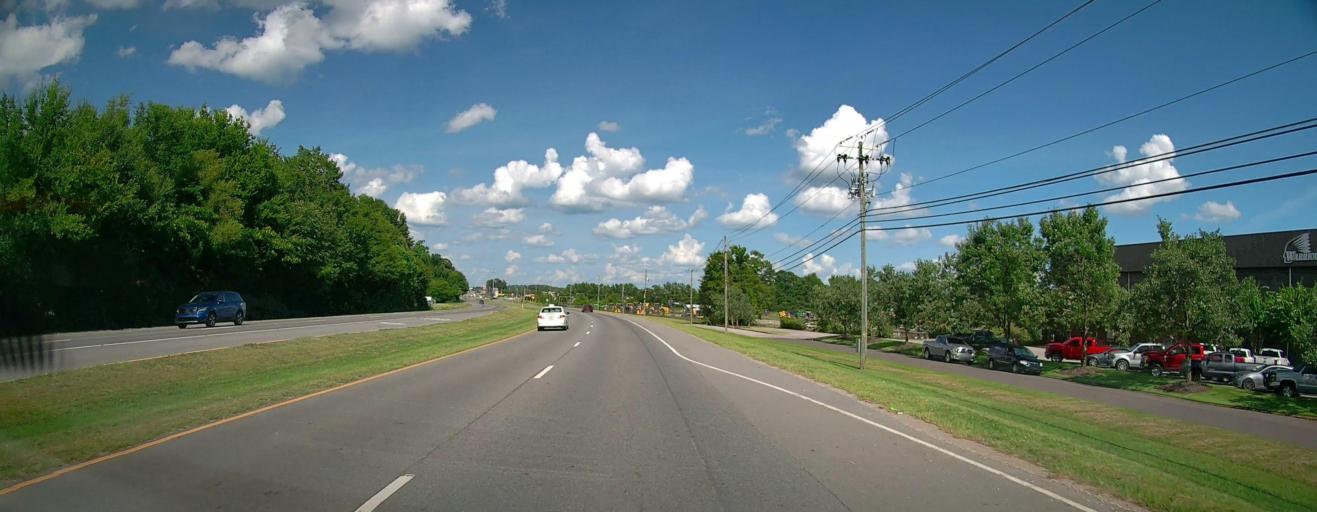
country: US
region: Alabama
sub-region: Tuscaloosa County
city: Northport
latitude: 33.2326
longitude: -87.6255
